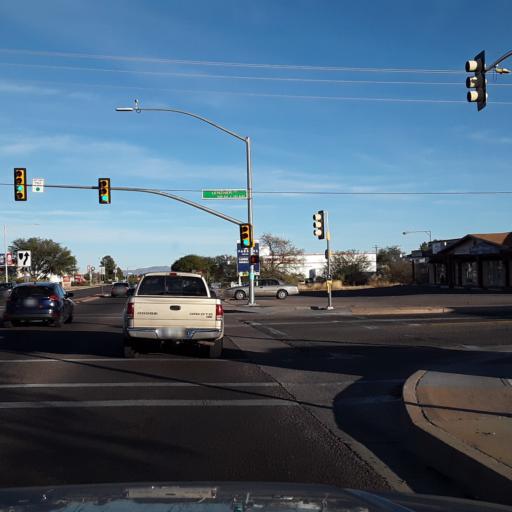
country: US
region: Arizona
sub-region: Cochise County
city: Sierra Vista
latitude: 31.5546
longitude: -110.2824
